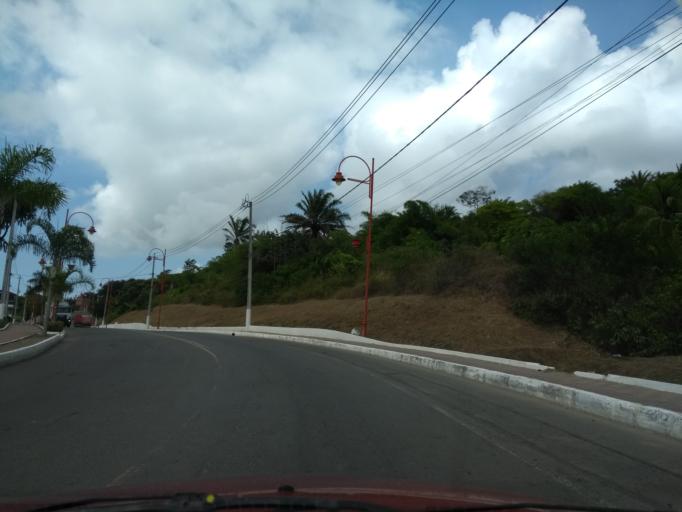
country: BR
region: Bahia
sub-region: Sao Francisco Do Conde
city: Sao Francisco do Conde
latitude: -12.6208
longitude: -38.6717
